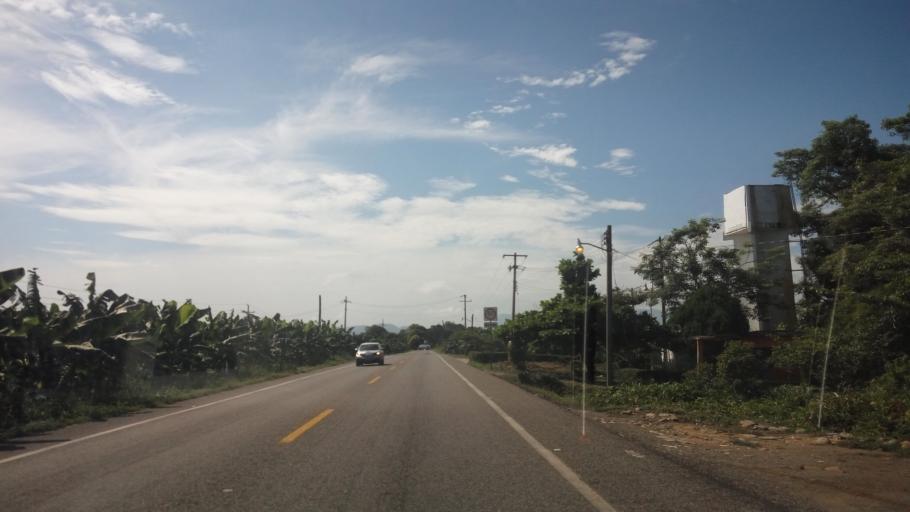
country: MX
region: Tabasco
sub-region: Teapa
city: Eureka y Belen
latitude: 17.6325
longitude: -92.9654
